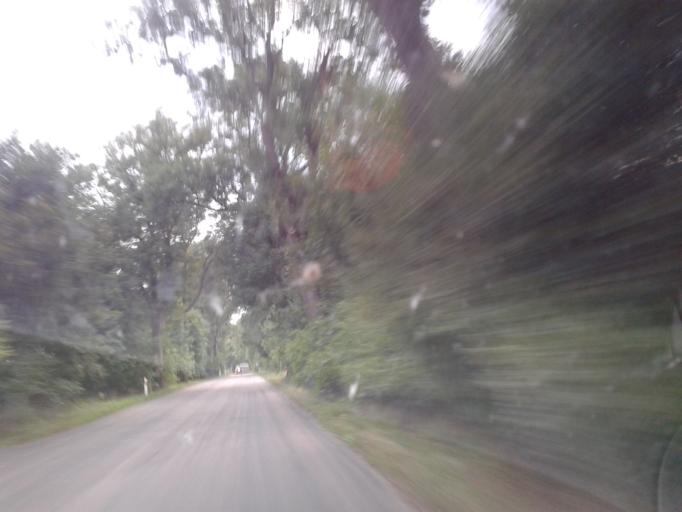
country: PL
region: West Pomeranian Voivodeship
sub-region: Powiat szczecinecki
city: Grzmiaca
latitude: 53.8484
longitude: 16.4560
